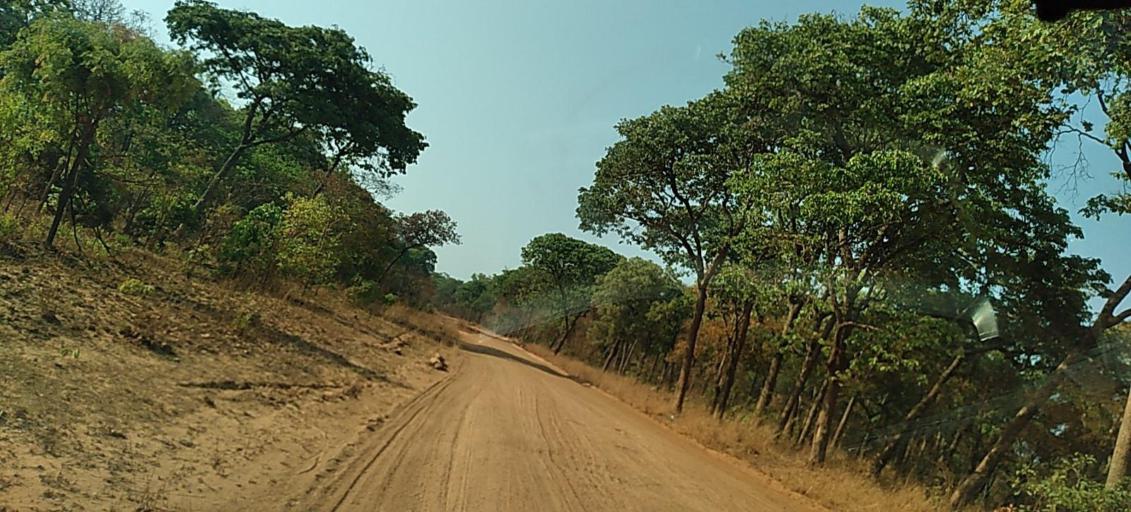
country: ZM
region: North-Western
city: Kasempa
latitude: -13.6624
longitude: 26.0104
